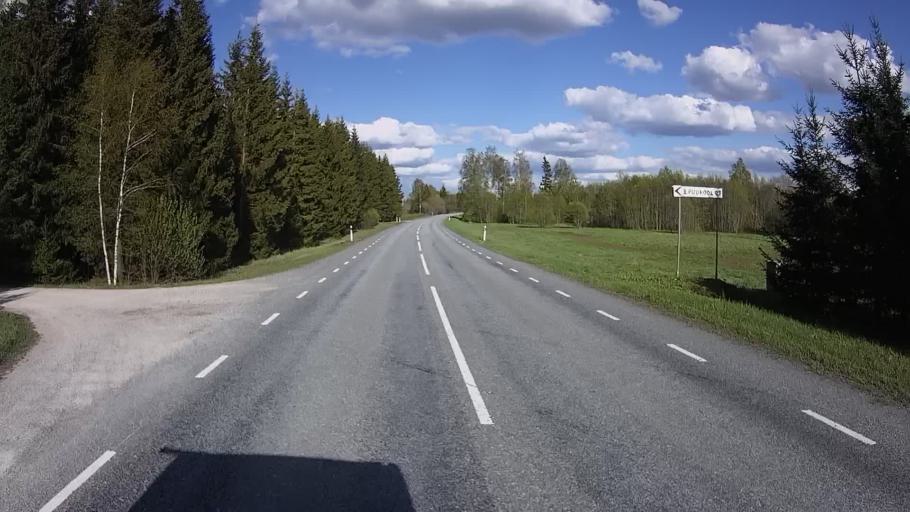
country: EE
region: Jogevamaa
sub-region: Poltsamaa linn
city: Poltsamaa
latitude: 58.6787
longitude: 26.0302
